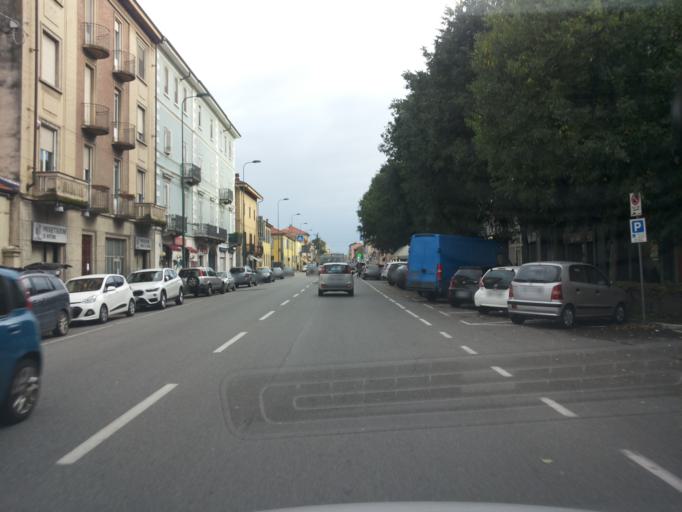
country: IT
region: Piedmont
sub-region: Provincia di Alessandria
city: Casale Monferrato
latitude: 45.1280
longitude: 8.4507
